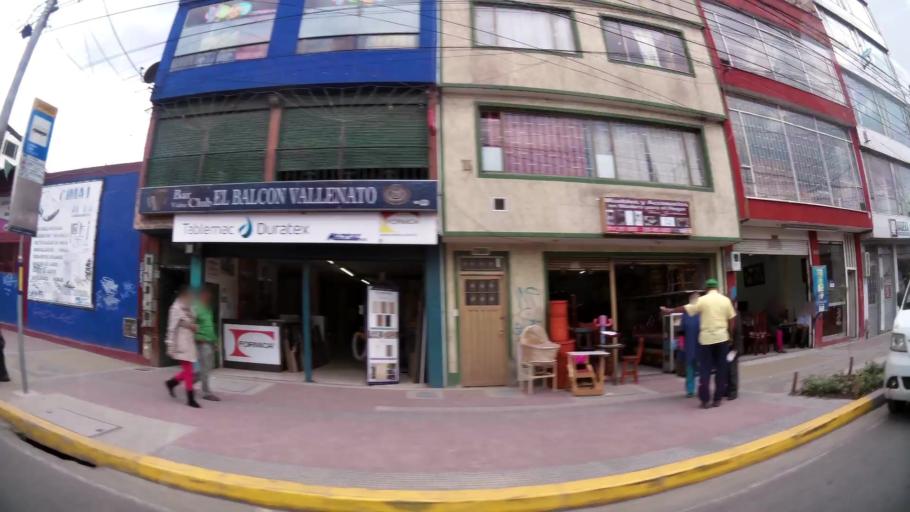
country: CO
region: Cundinamarca
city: Cota
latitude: 4.7407
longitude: -74.0957
